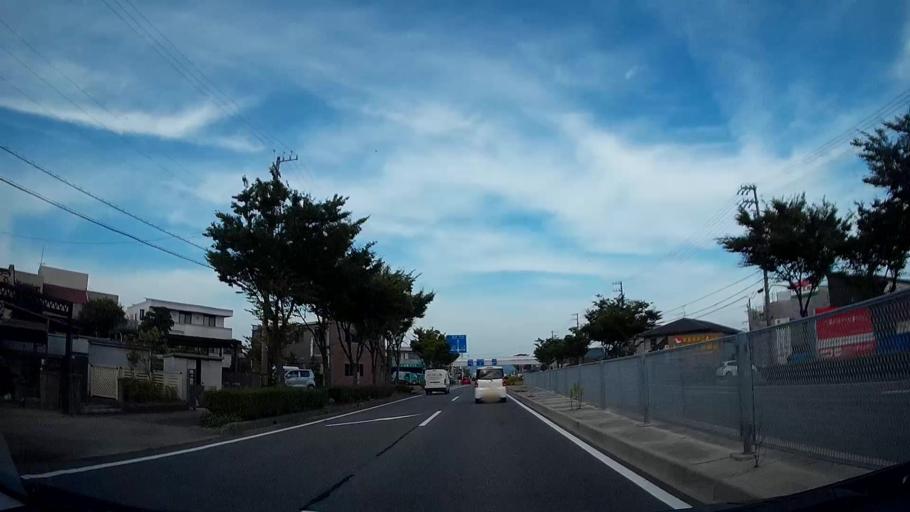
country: JP
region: Aichi
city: Nishio
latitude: 34.8485
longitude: 137.0245
